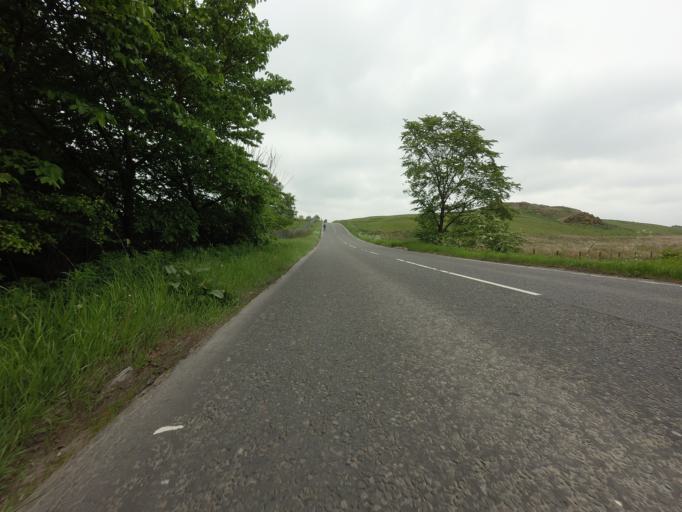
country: GB
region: Scotland
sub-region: Fife
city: Townhill
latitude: 56.1122
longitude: -3.4484
